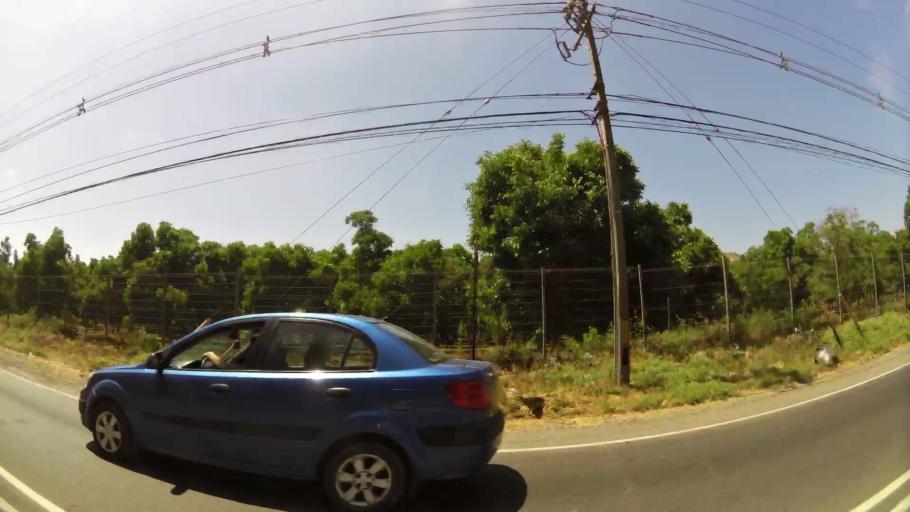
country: CL
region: Santiago Metropolitan
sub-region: Provincia de Maipo
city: San Bernardo
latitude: -33.5632
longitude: -70.7606
